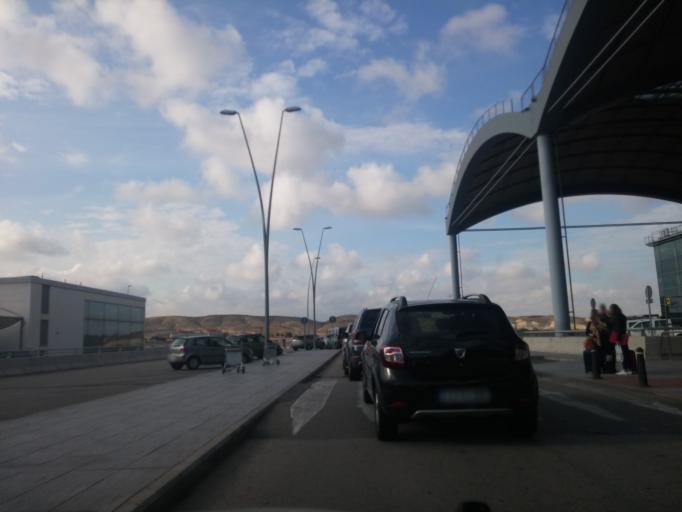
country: ES
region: Valencia
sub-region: Provincia de Alicante
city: Alicante
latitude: 38.2879
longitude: -0.5530
